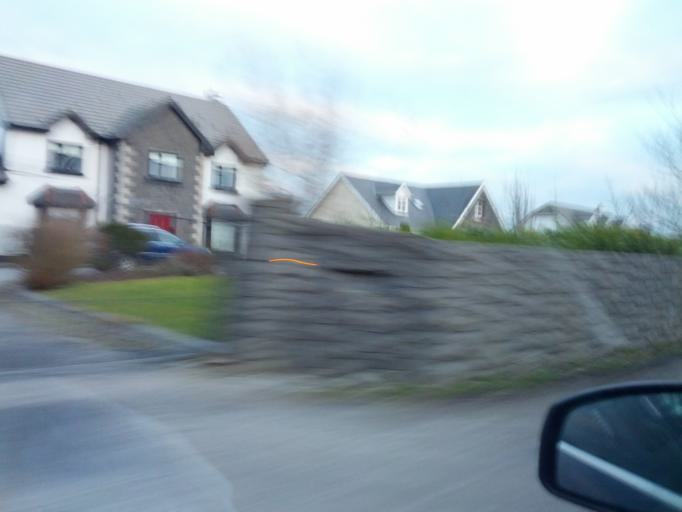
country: IE
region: Connaught
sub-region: County Galway
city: Athenry
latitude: 53.3283
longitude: -8.7663
